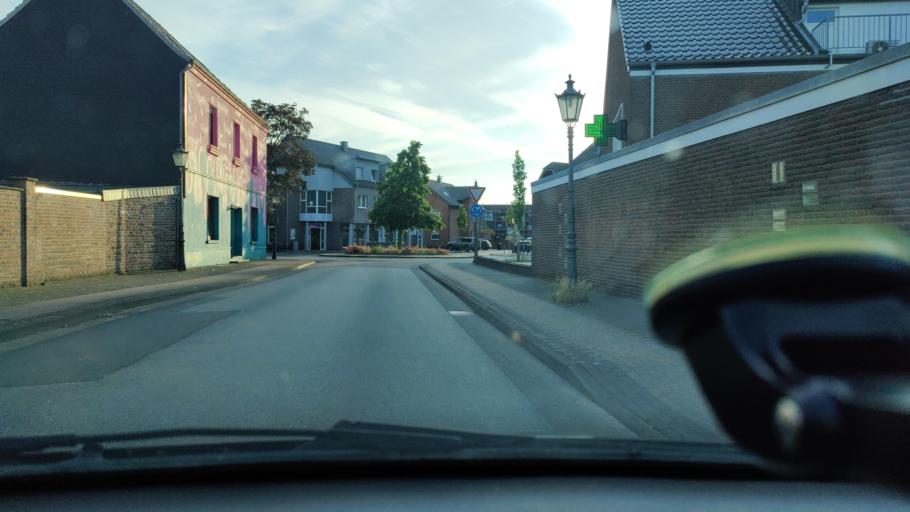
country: DE
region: North Rhine-Westphalia
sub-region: Regierungsbezirk Dusseldorf
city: Issum
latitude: 51.4932
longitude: 6.4304
